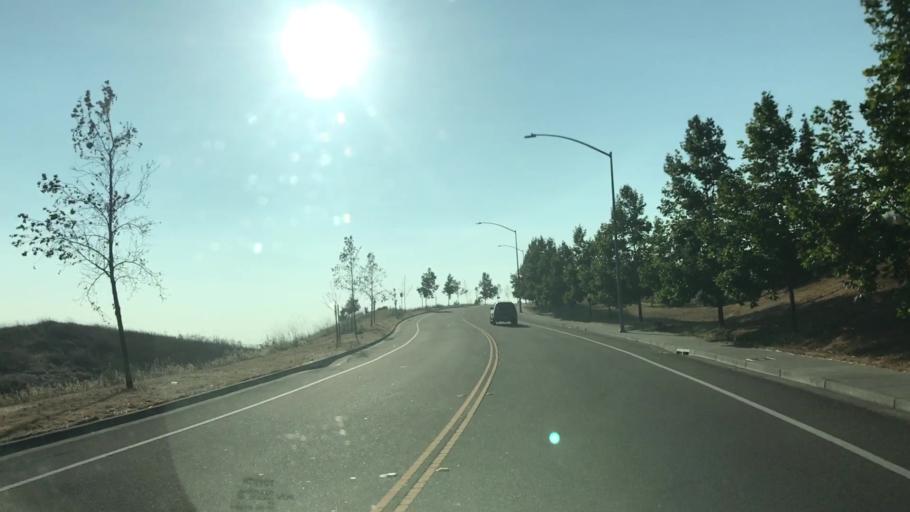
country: US
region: California
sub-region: Alameda County
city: Dublin
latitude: 37.6989
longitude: -121.9723
